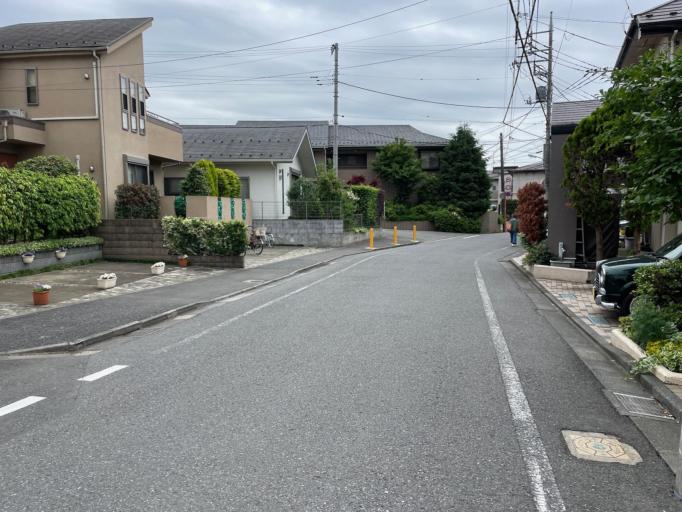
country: JP
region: Tokyo
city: Chofugaoka
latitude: 35.6561
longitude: 139.5818
